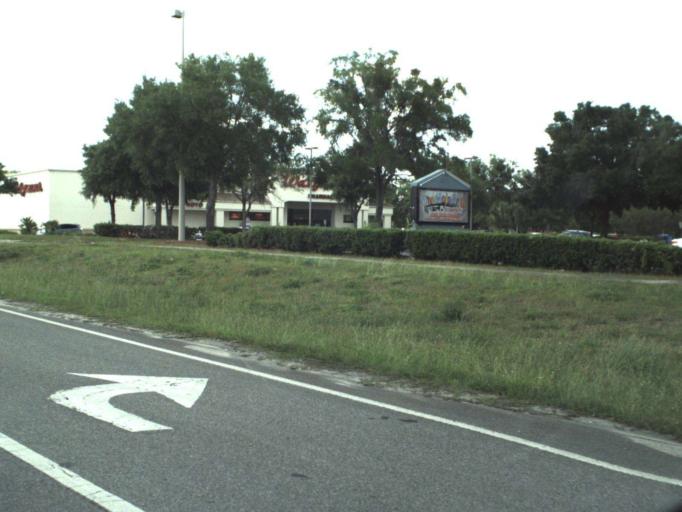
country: US
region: Florida
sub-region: Marion County
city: Ocala
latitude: 29.1722
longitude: -82.1585
